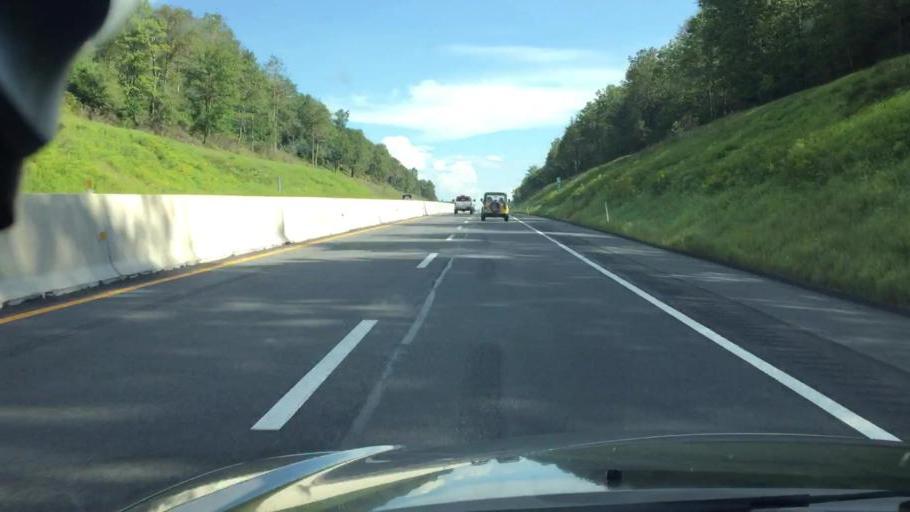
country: US
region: Pennsylvania
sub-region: Luzerne County
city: White Haven
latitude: 41.0624
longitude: -75.6876
